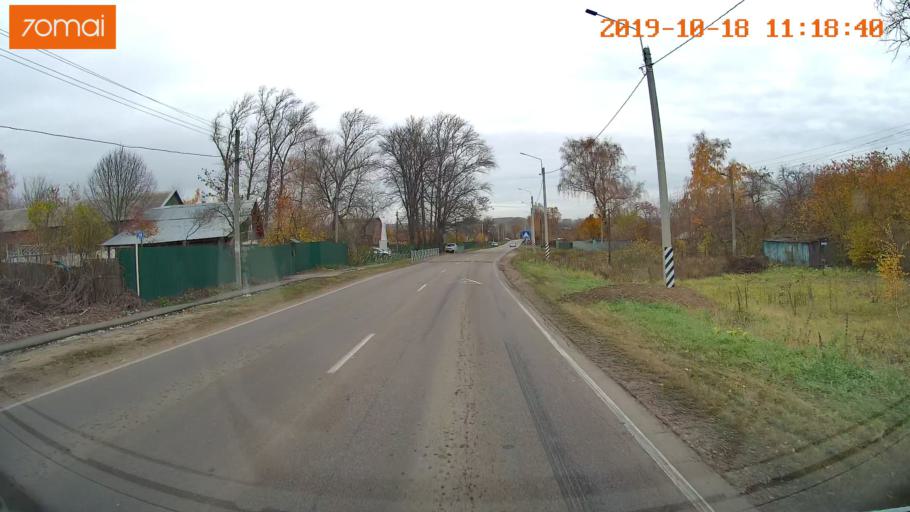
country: RU
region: Tula
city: Kimovsk
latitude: 54.0408
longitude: 38.5508
